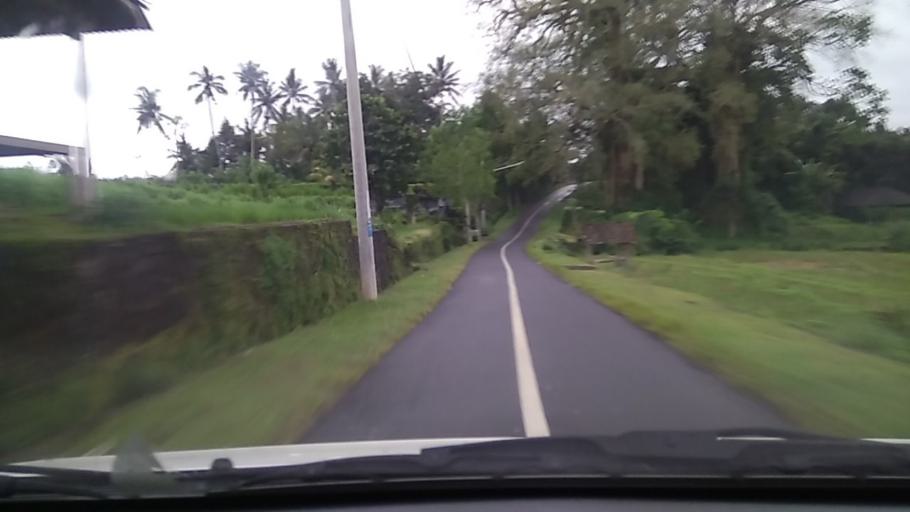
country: ID
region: Bali
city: Tiyingtali Kelod
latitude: -8.4022
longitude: 115.6175
